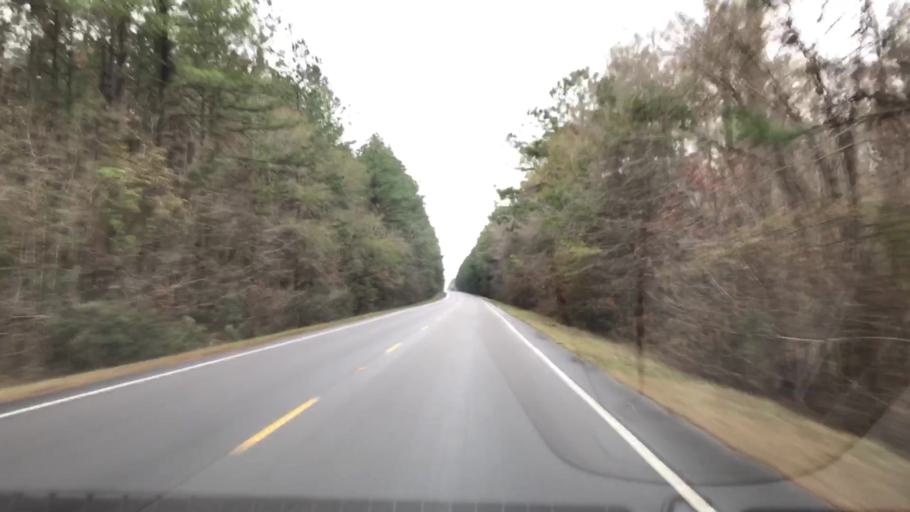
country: US
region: South Carolina
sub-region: Berkeley County
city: Saint Stephen
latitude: 33.2901
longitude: -79.7948
